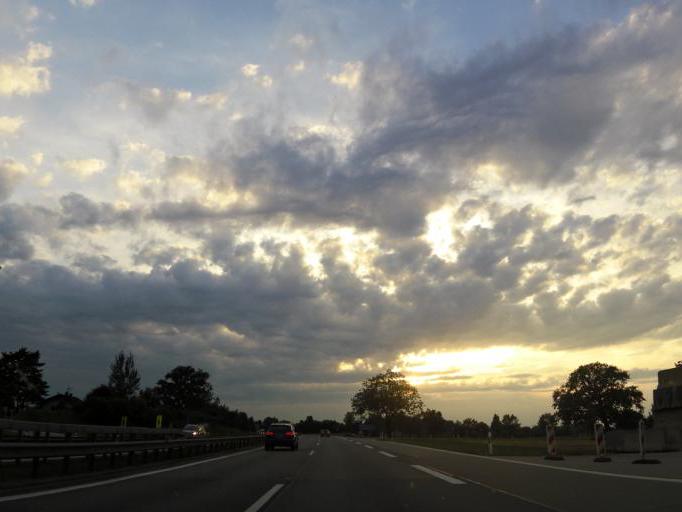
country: DE
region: Bavaria
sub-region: Upper Bavaria
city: Ubersee
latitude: 47.8379
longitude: 12.4898
